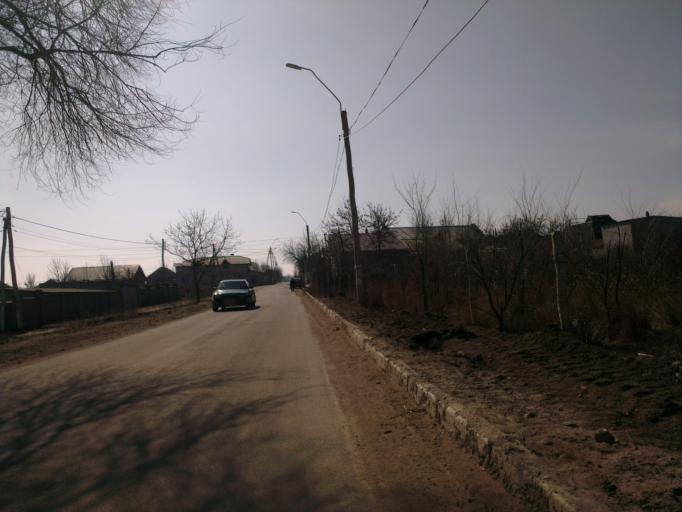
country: MD
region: Chisinau
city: Ciorescu
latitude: 47.1246
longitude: 28.8844
